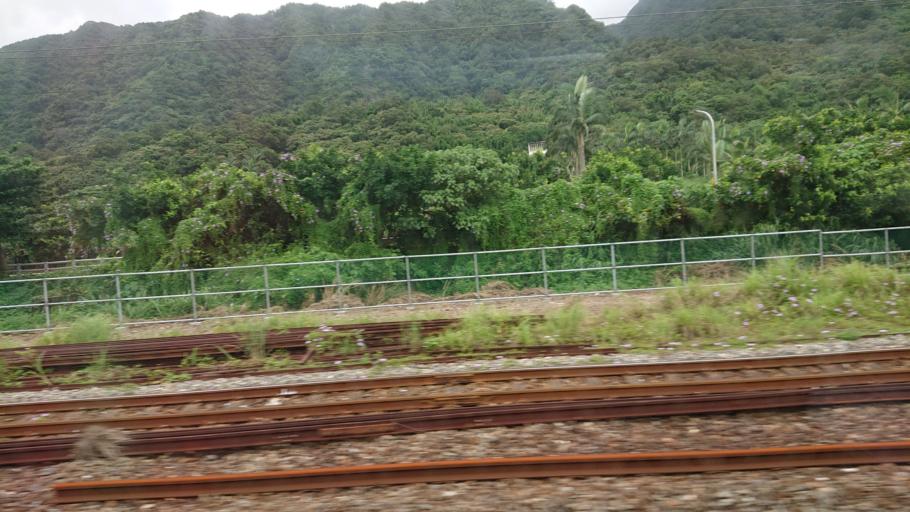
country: TW
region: Taiwan
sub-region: Keelung
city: Keelung
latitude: 24.9647
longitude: 121.9212
